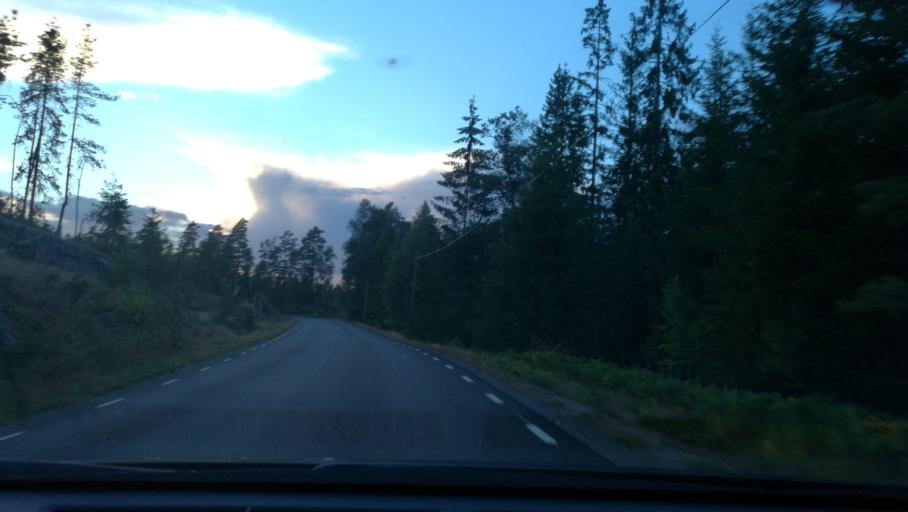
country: SE
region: OEstergoetland
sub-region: Norrkopings Kommun
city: Jursla
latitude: 58.8009
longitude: 16.1444
